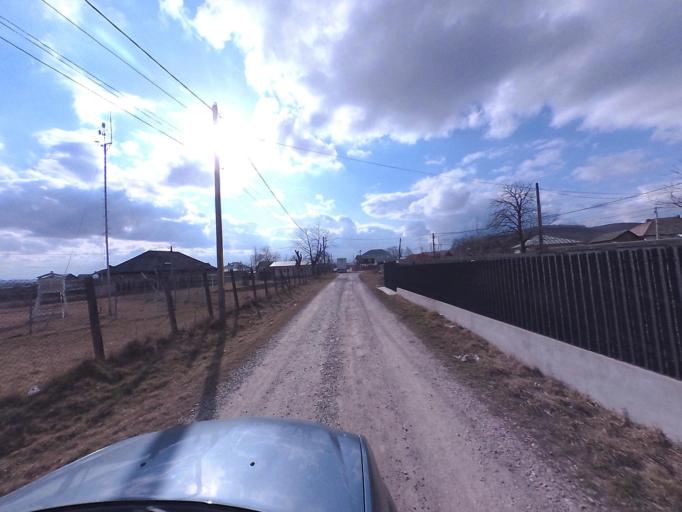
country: RO
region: Neamt
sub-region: Oras Targu Neamt
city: Targu Neamt
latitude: 47.2125
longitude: 26.3790
